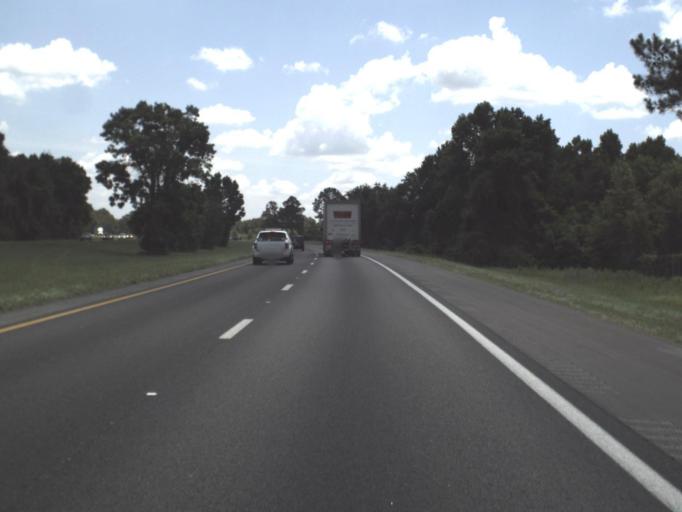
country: US
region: Florida
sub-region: Madison County
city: Madison
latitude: 30.4153
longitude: -83.4348
